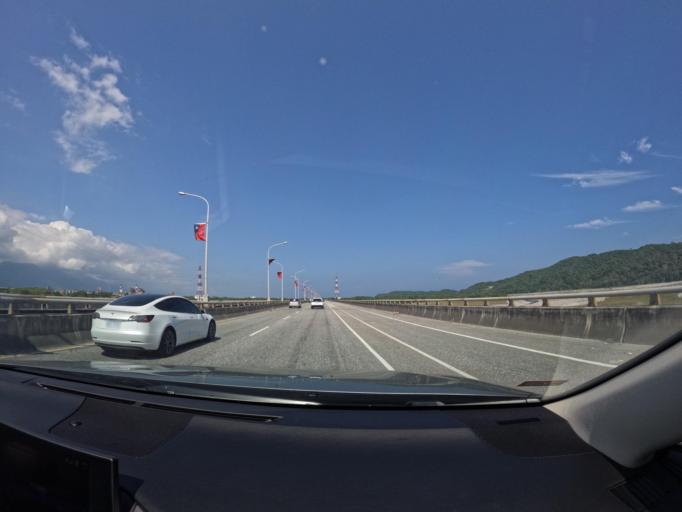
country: TW
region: Taiwan
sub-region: Hualien
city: Hualian
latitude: 23.9170
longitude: 121.5824
